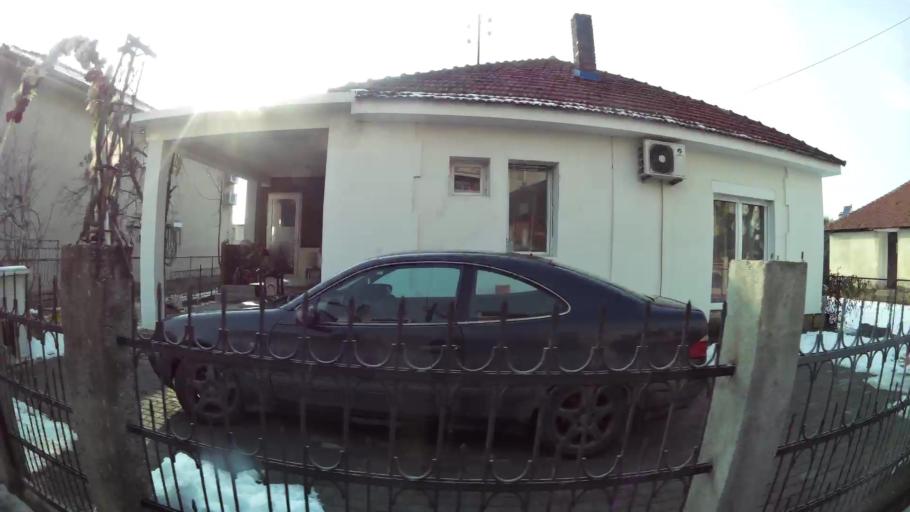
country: MK
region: Ilinden
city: Marino
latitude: 41.9875
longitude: 21.5856
